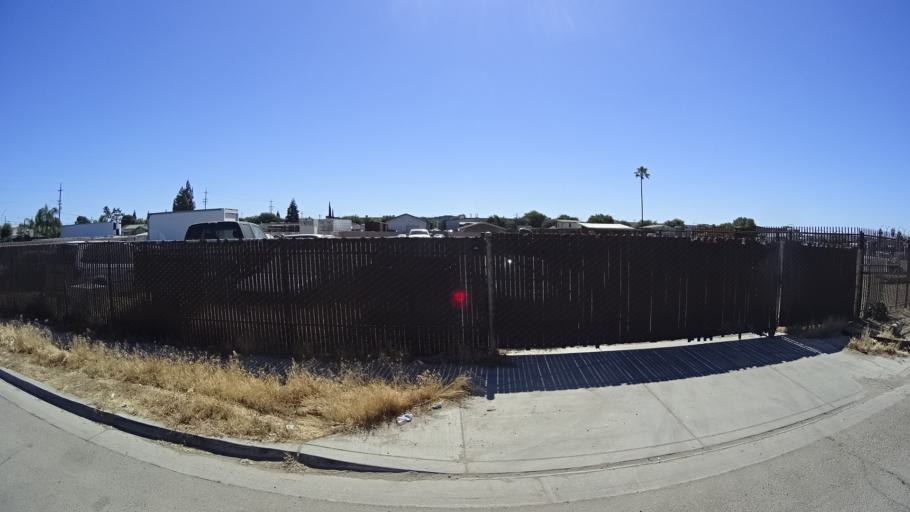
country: US
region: California
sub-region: Fresno County
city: Easton
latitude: 36.6986
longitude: -119.7931
